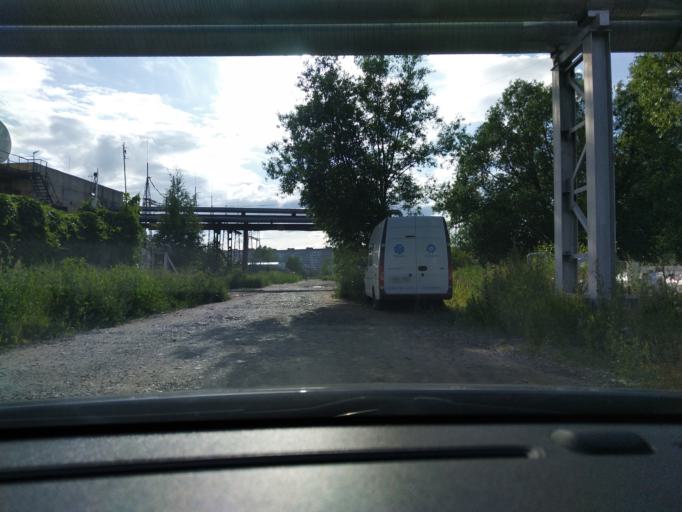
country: RU
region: St.-Petersburg
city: Gorelovo
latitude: 59.7847
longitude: 30.1600
